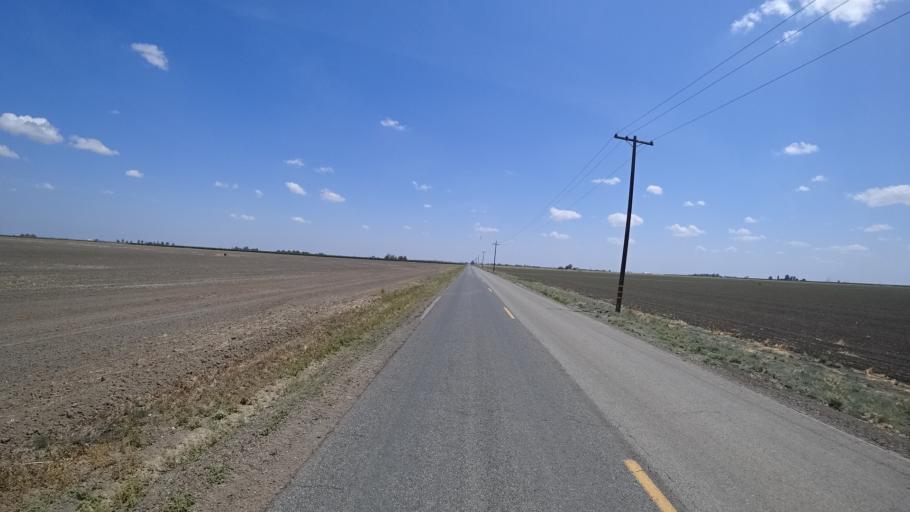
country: US
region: California
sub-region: Kings County
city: Stratford
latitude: 36.1895
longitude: -119.8678
